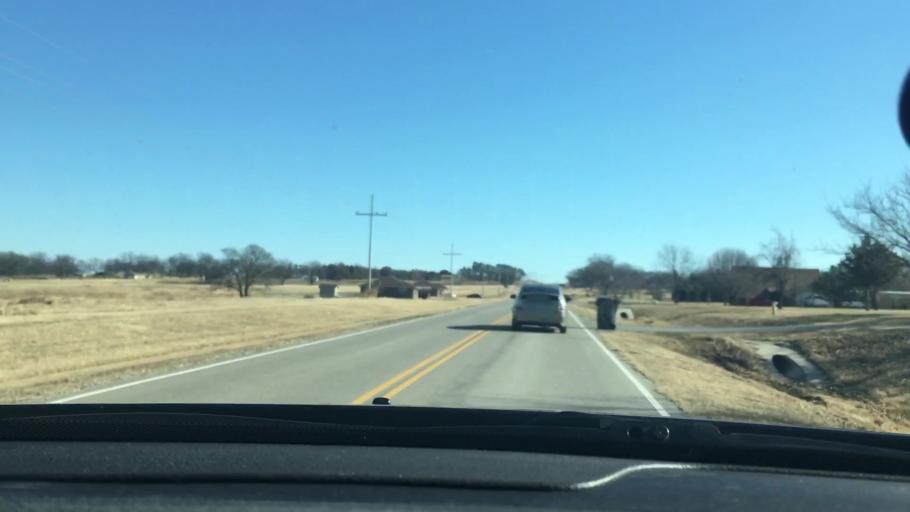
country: US
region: Oklahoma
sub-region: Murray County
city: Davis
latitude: 34.4772
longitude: -97.0641
